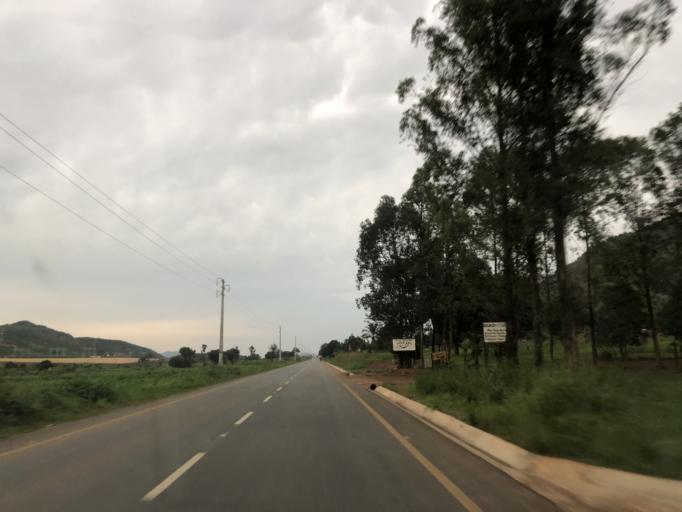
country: AO
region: Cuanza Sul
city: Uacu Cungo
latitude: -11.3164
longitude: 15.0836
